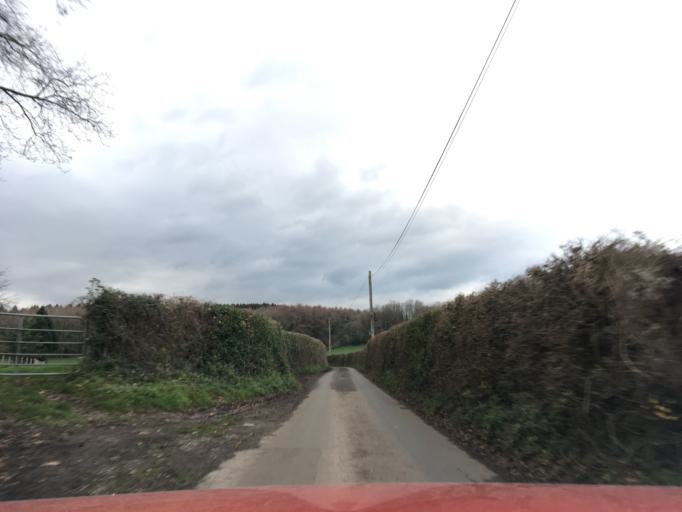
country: GB
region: Wales
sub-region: Monmouthshire
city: Rogiet
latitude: 51.5979
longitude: -2.7749
